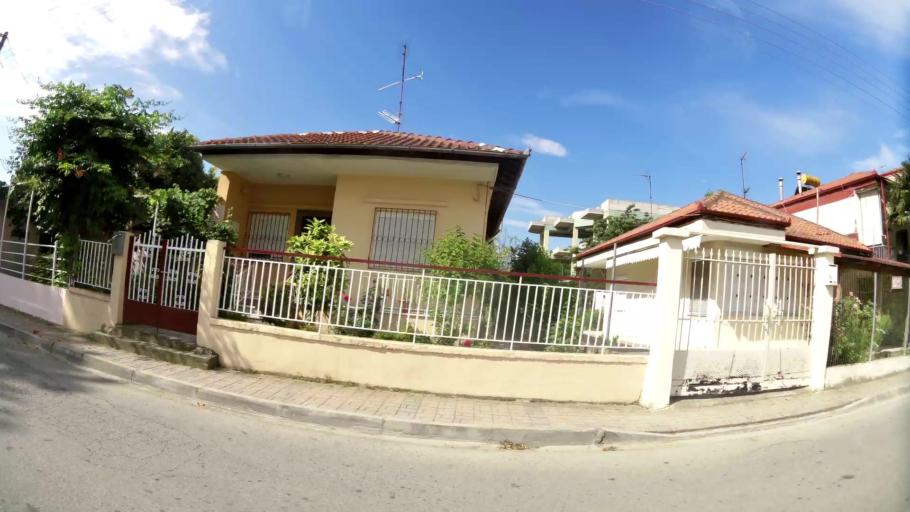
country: GR
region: Central Macedonia
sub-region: Nomos Pierias
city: Katerini
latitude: 40.2779
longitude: 22.5111
